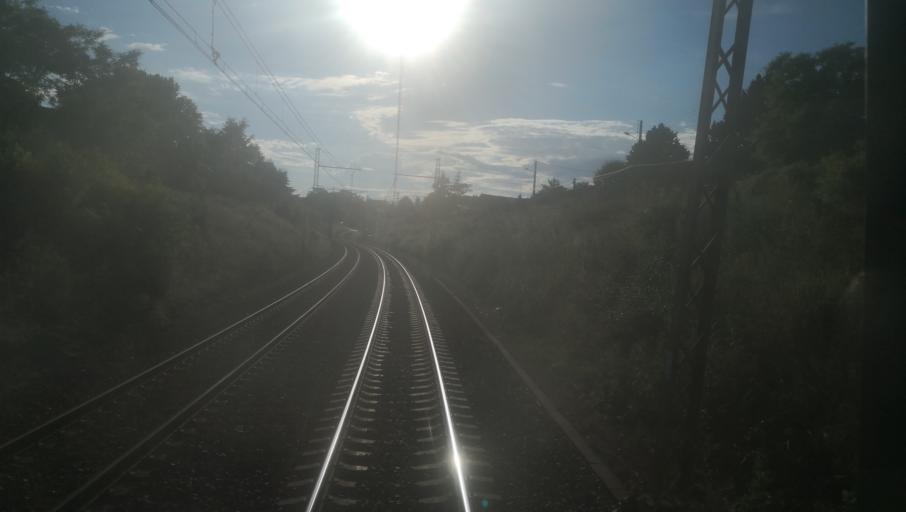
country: FR
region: Centre
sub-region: Departement du Cher
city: Vierzon
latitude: 47.2209
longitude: 2.0865
